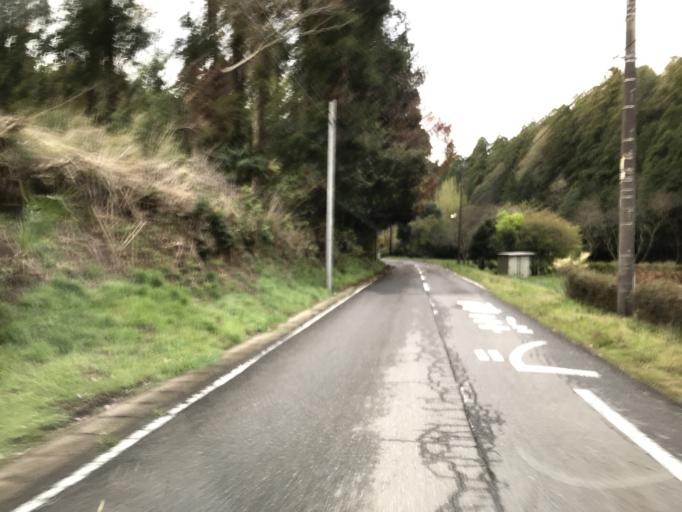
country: JP
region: Chiba
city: Yokaichiba
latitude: 35.7698
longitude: 140.4594
